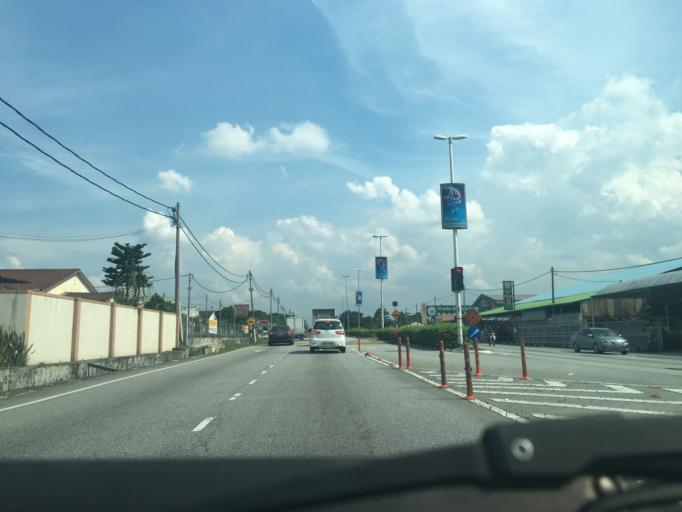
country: MY
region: Perak
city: Ipoh
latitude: 4.6191
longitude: 101.0803
